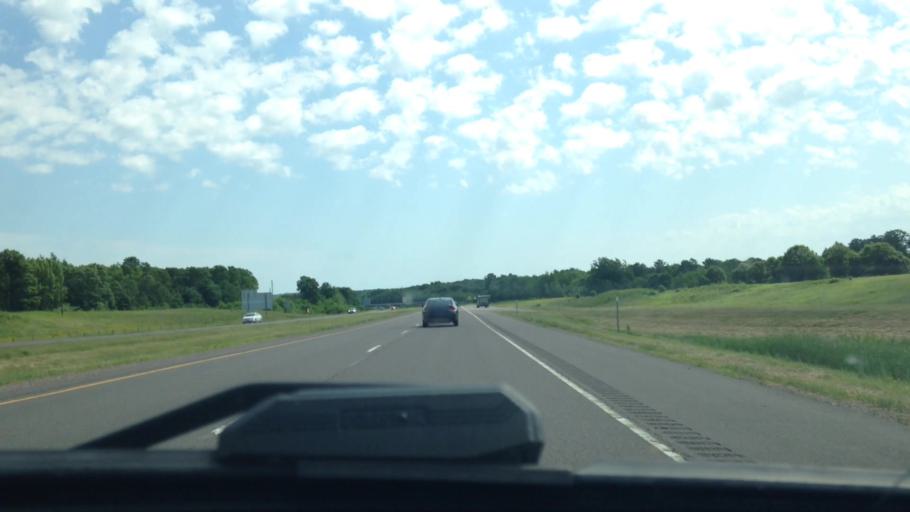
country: US
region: Wisconsin
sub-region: Washburn County
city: Spooner
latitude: 45.8564
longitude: -91.8555
